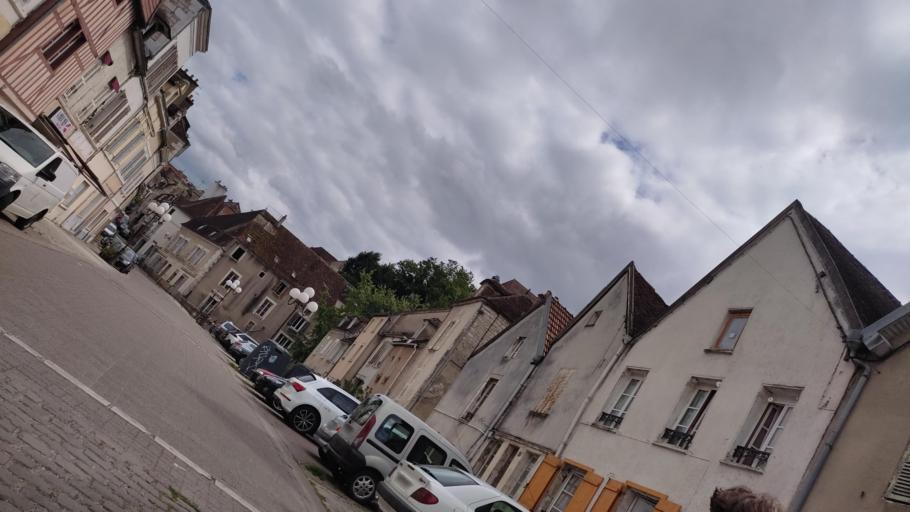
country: FR
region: Bourgogne
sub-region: Departement de l'Yonne
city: Tonnerre
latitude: 47.8576
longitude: 3.9706
